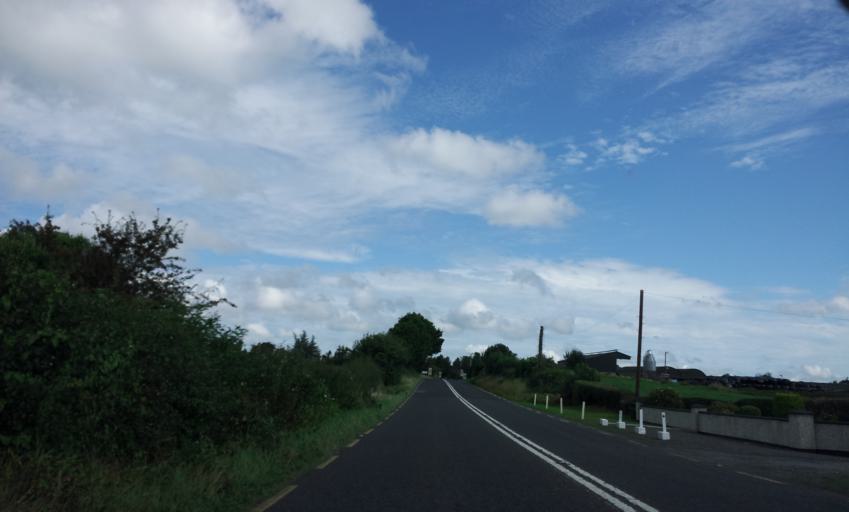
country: IE
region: Leinster
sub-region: Laois
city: Mountrath
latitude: 52.9891
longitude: -7.4876
